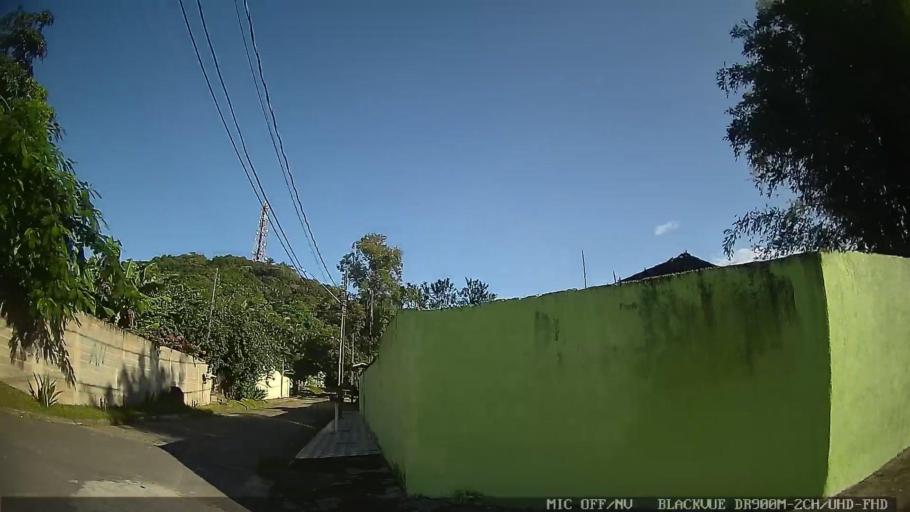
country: BR
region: Sao Paulo
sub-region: Peruibe
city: Peruibe
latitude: -24.2724
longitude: -46.9490
